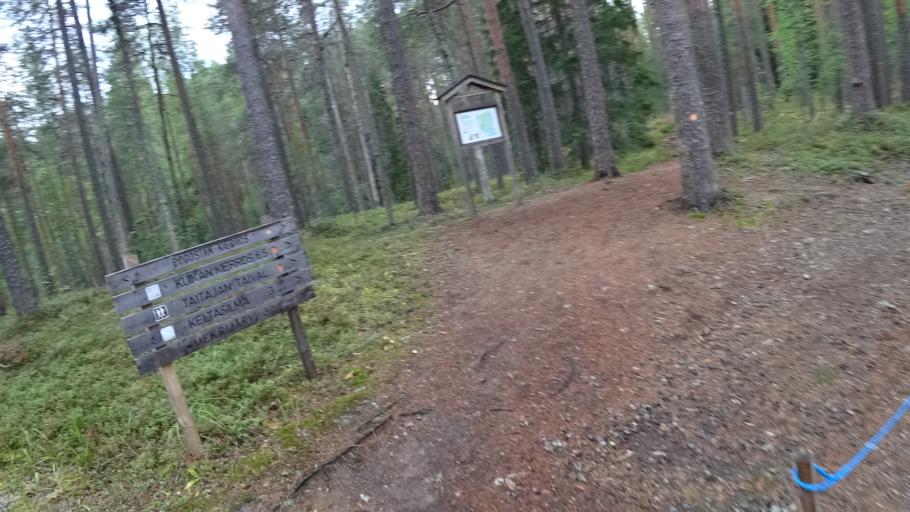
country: FI
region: North Karelia
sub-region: Joensuu
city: Ilomantsi
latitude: 62.5800
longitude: 31.1741
